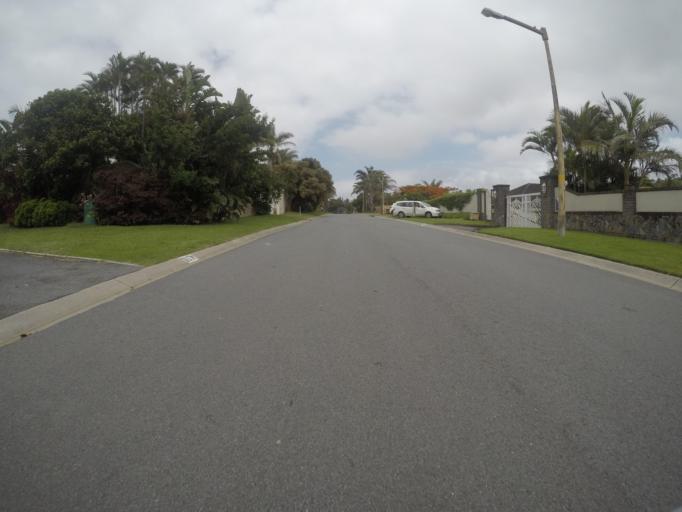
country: ZA
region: Eastern Cape
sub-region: Buffalo City Metropolitan Municipality
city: East London
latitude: -32.9916
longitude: 27.9380
